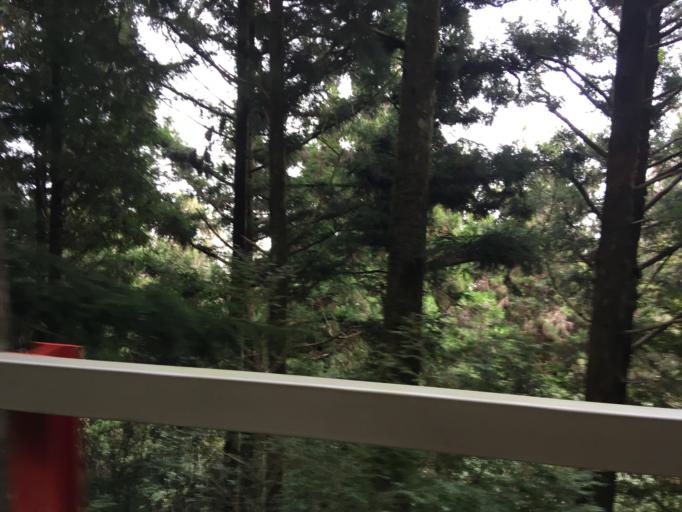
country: TW
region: Taiwan
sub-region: Yilan
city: Yilan
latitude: 24.4800
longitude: 121.5368
